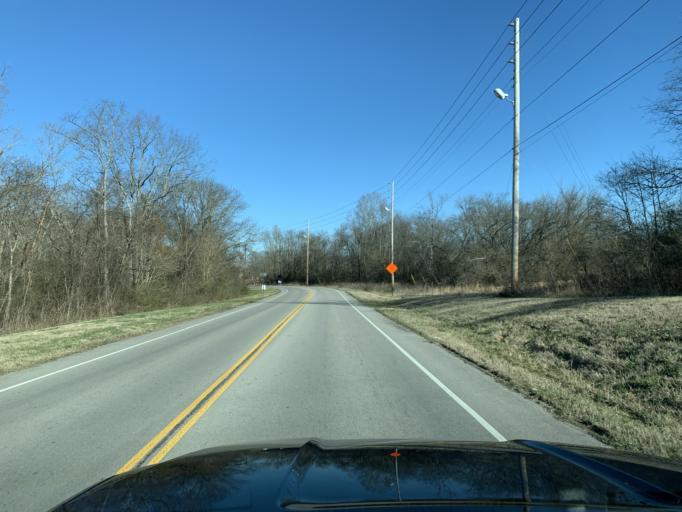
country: US
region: Tennessee
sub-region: Maury County
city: Spring Hill
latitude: 35.7502
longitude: -86.9217
